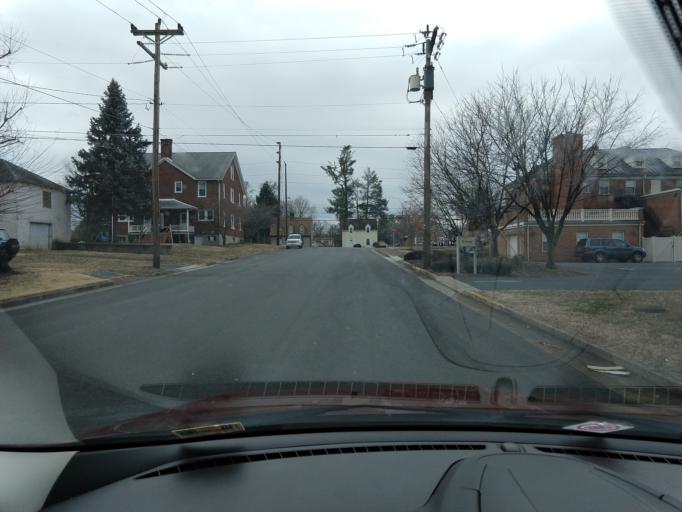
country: US
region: Virginia
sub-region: City of Waynesboro
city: Waynesboro
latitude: 38.0746
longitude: -78.9041
